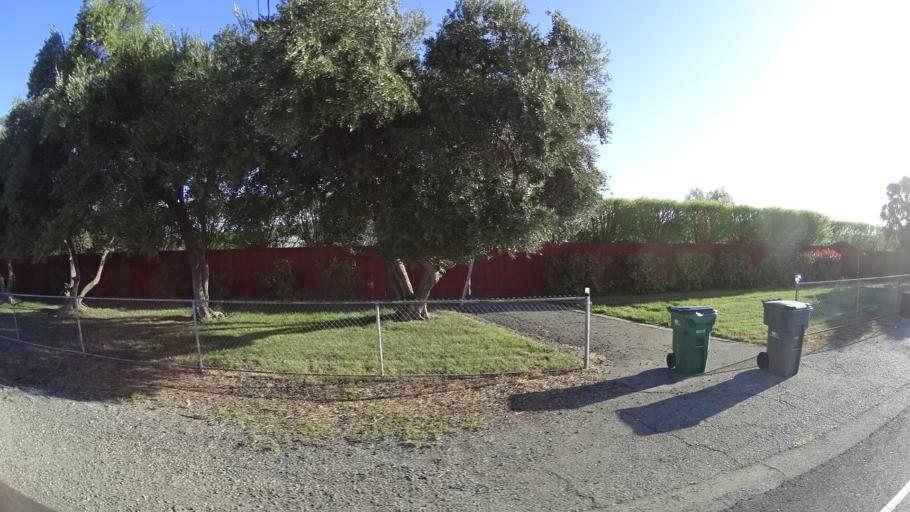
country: US
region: California
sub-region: Glenn County
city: Orland
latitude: 39.7619
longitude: -122.2337
